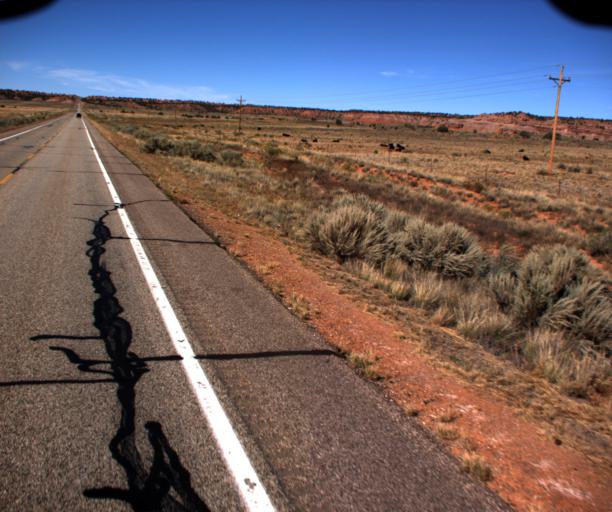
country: US
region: Arizona
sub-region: Mohave County
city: Colorado City
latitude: 36.8734
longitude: -112.8658
